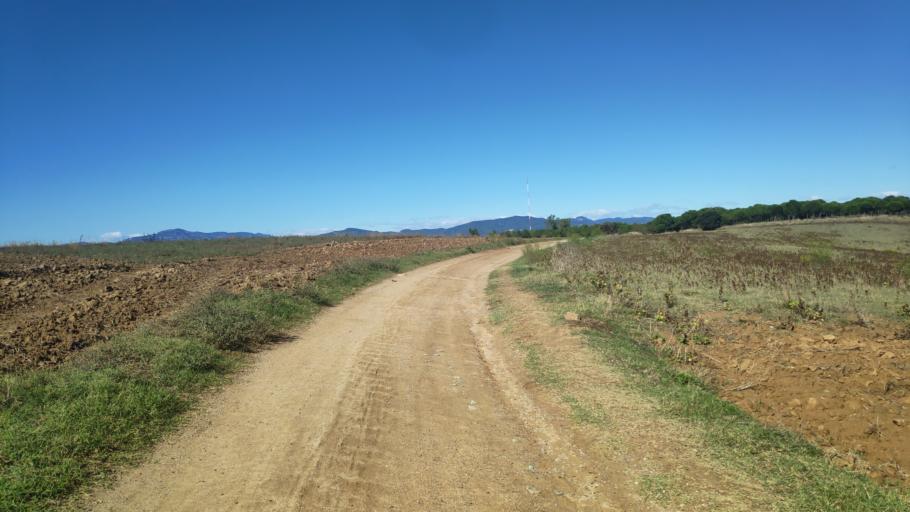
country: ES
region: Catalonia
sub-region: Provincia de Barcelona
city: Mollet del Valles
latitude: 41.5410
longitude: 2.2000
